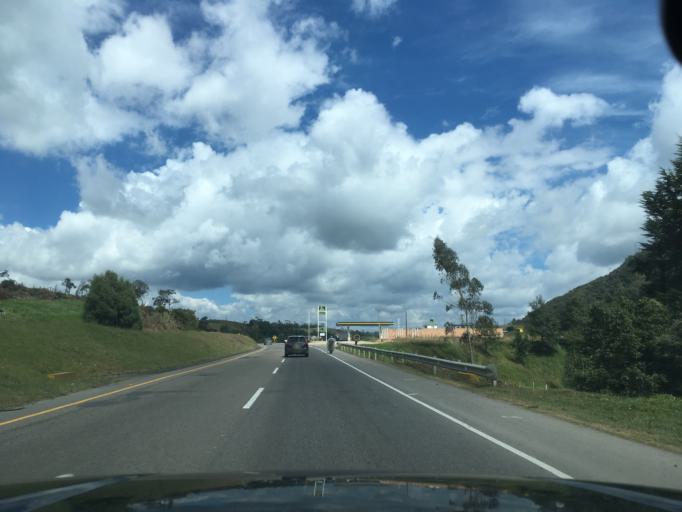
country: CO
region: Boyaca
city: Ventaquemada
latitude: 5.4025
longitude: -73.4789
